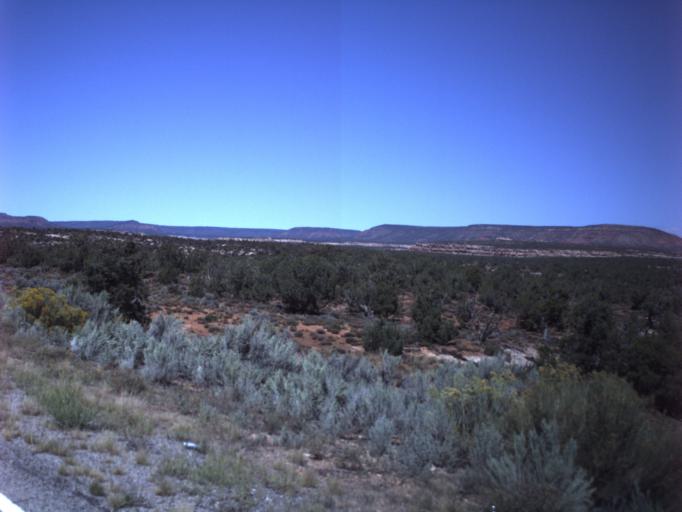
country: US
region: Utah
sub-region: San Juan County
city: Blanding
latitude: 37.5263
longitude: -109.6795
